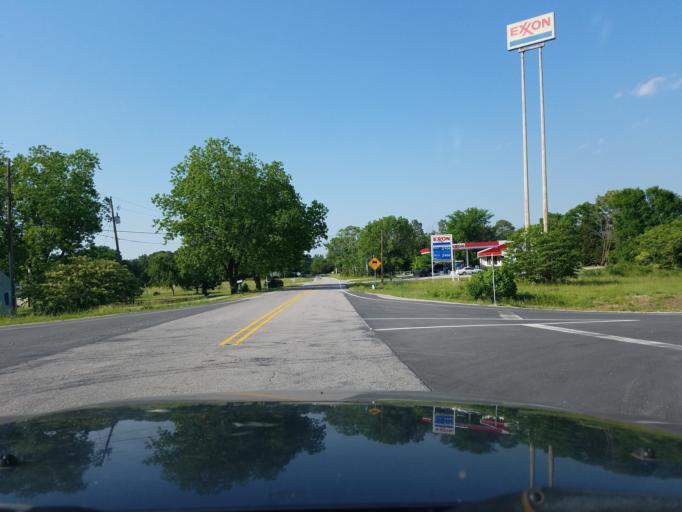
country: US
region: North Carolina
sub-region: Vance County
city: Henderson
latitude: 36.3629
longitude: -78.3742
